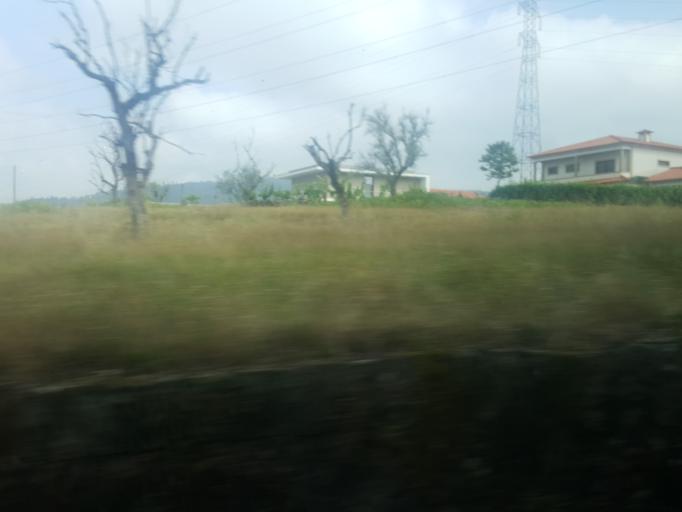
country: PT
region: Porto
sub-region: Penafiel
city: Perafita
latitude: 41.1595
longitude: -8.2113
